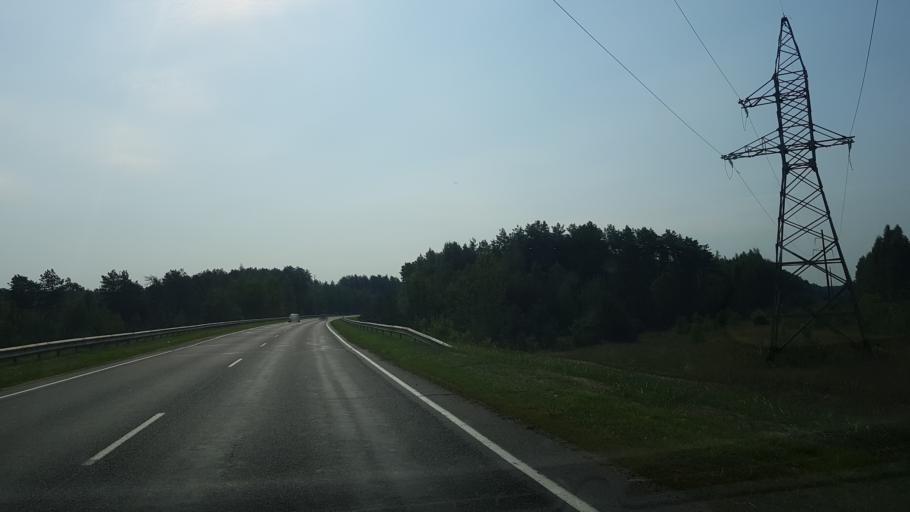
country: BY
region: Mogilev
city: Babruysk
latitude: 53.1626
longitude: 29.3053
